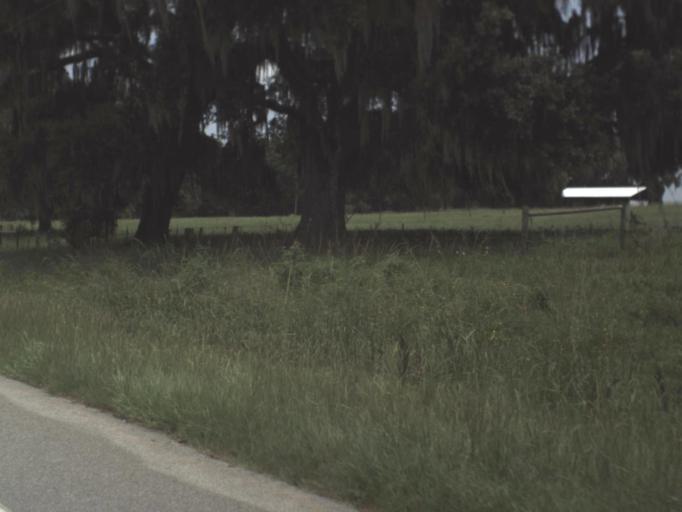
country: US
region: Florida
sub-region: Madison County
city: Madison
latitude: 30.5130
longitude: -83.4227
